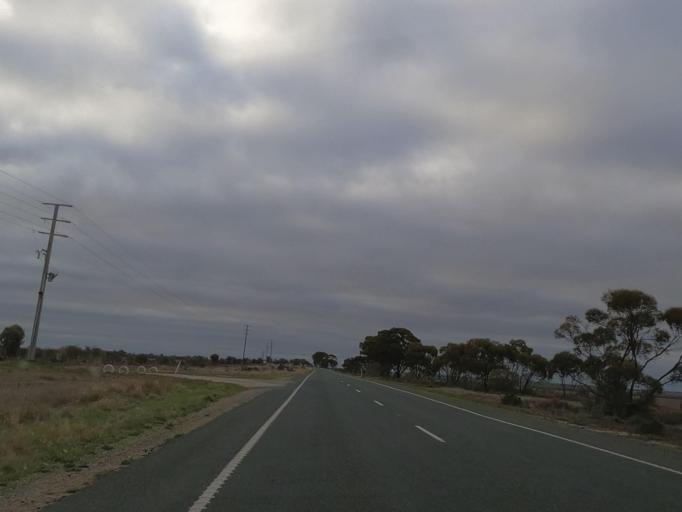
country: AU
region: Victoria
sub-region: Swan Hill
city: Swan Hill
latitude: -35.5784
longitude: 143.7886
